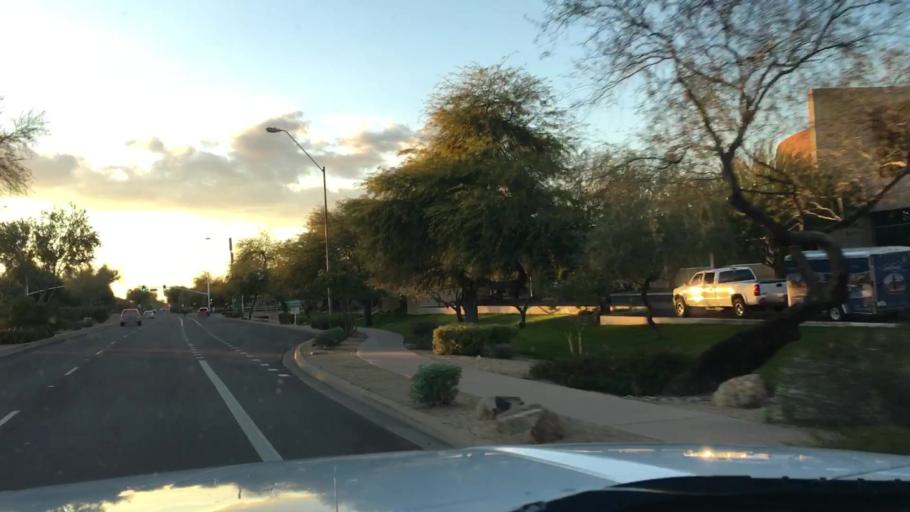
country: US
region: Arizona
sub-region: Maricopa County
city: Paradise Valley
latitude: 33.6402
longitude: -111.8946
